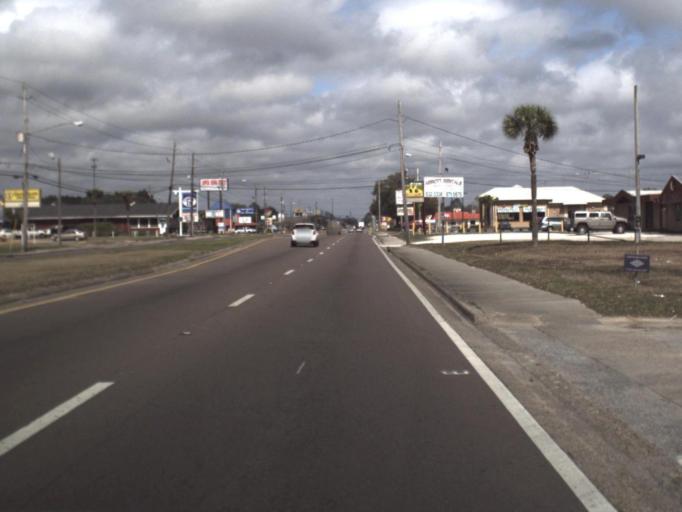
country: US
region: Florida
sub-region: Bay County
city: Parker
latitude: 30.1408
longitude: -85.5911
